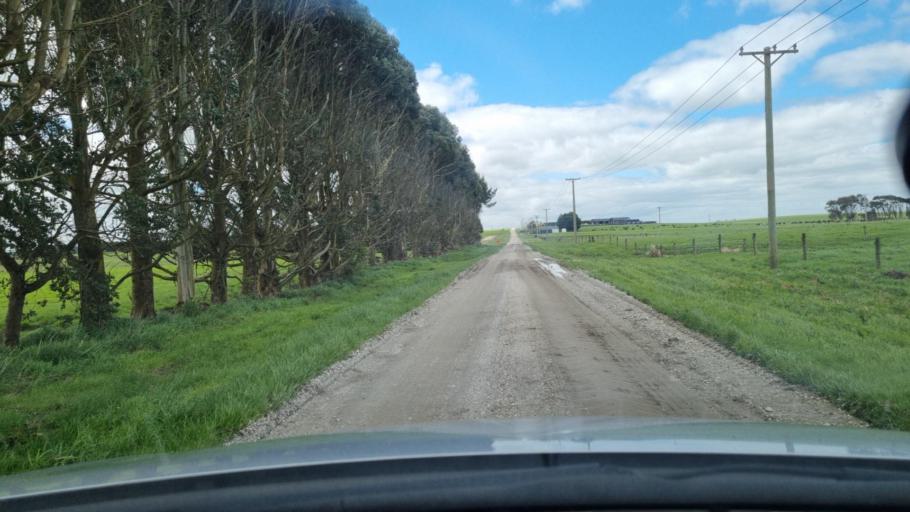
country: NZ
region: Southland
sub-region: Invercargill City
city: Invercargill
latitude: -46.4506
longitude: 168.4081
